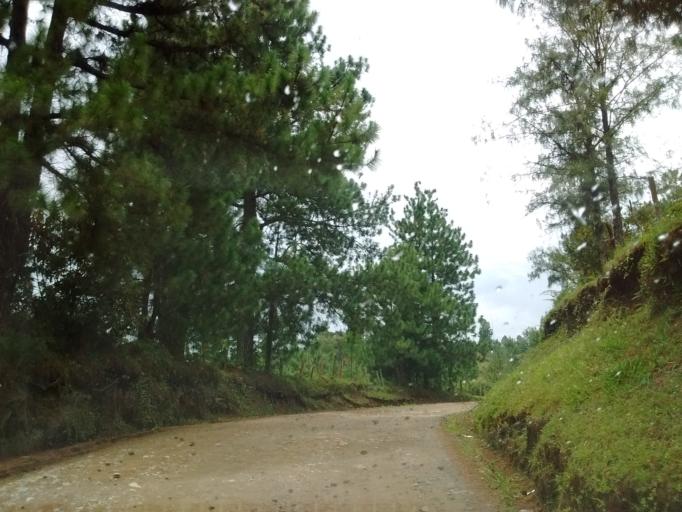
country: CO
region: Cauca
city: Cajibio
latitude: 2.5682
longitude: -76.6384
